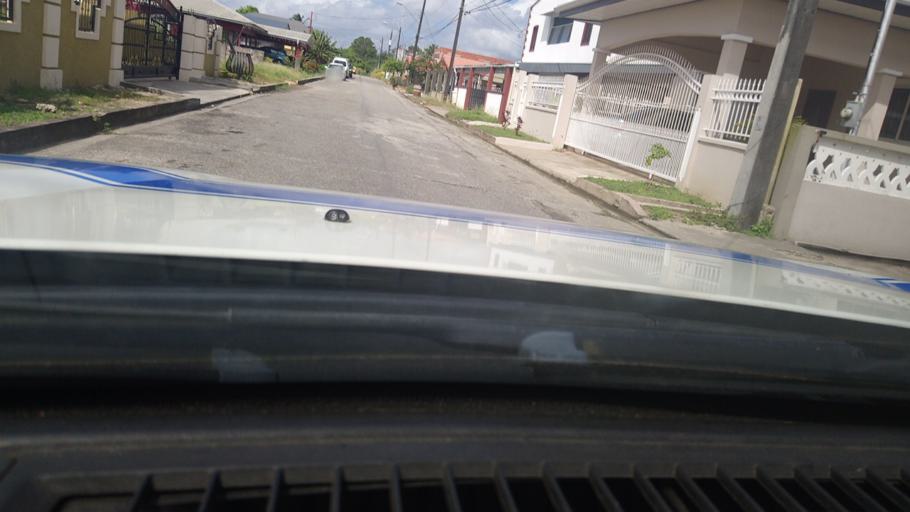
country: TT
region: Borough of Arima
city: Arima
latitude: 10.6174
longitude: -61.2979
